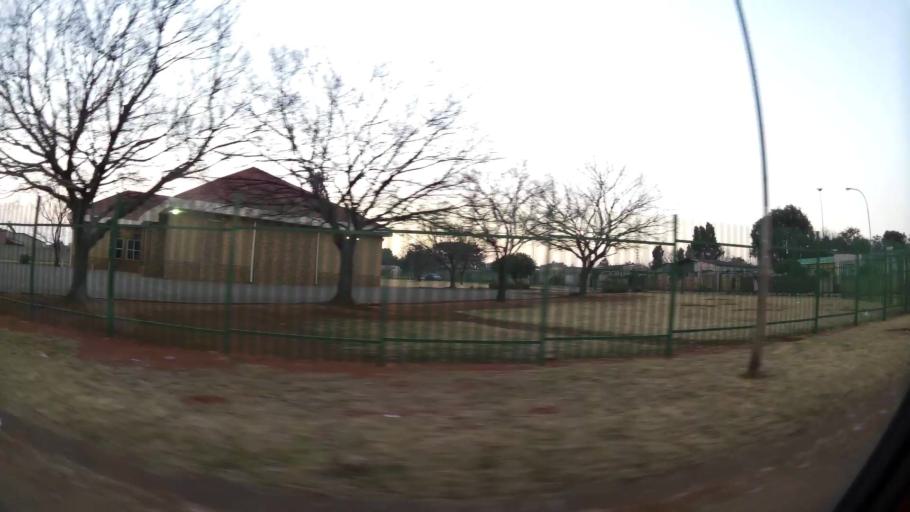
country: ZA
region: Gauteng
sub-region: City of Johannesburg Metropolitan Municipality
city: Soweto
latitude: -26.2899
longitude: 27.8756
